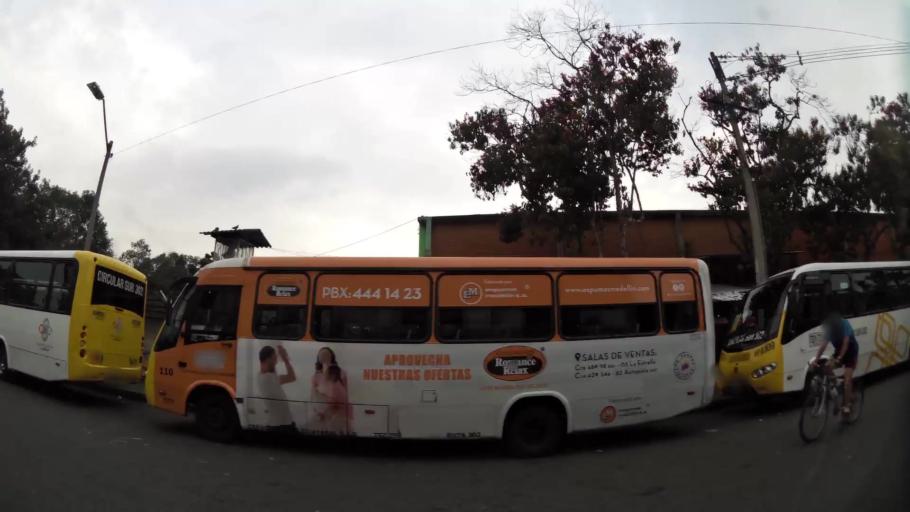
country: CO
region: Antioquia
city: Medellin
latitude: 6.2514
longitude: -75.5988
